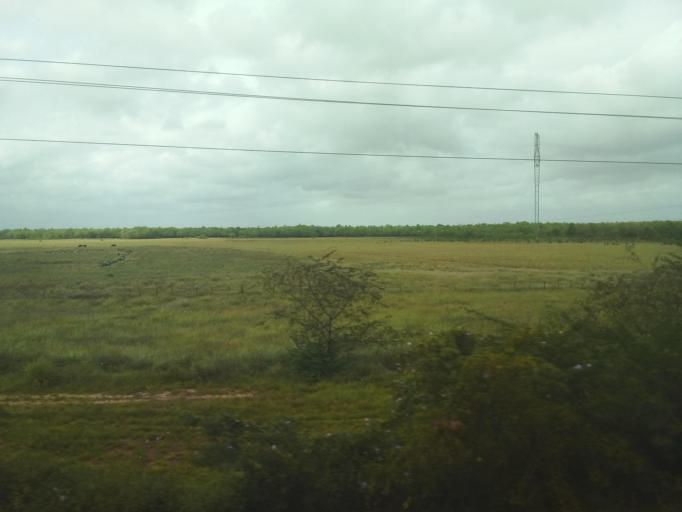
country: BR
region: Maranhao
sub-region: Icatu
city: Icatu
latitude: -2.9114
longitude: -44.3563
